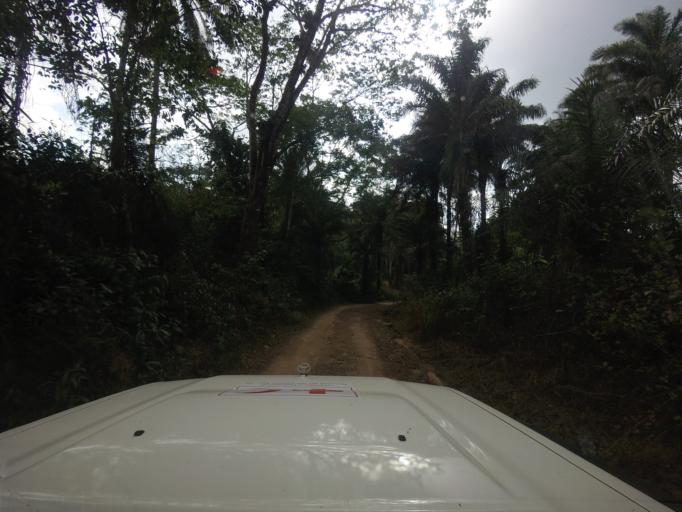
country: LR
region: Lofa
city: Voinjama
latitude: 8.3935
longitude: -9.6355
